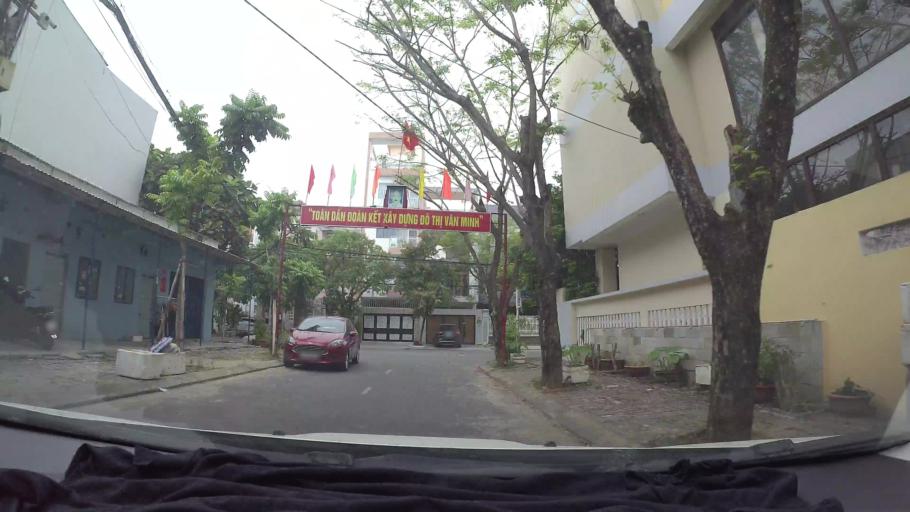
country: VN
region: Da Nang
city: Cam Le
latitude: 16.0390
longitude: 108.2149
